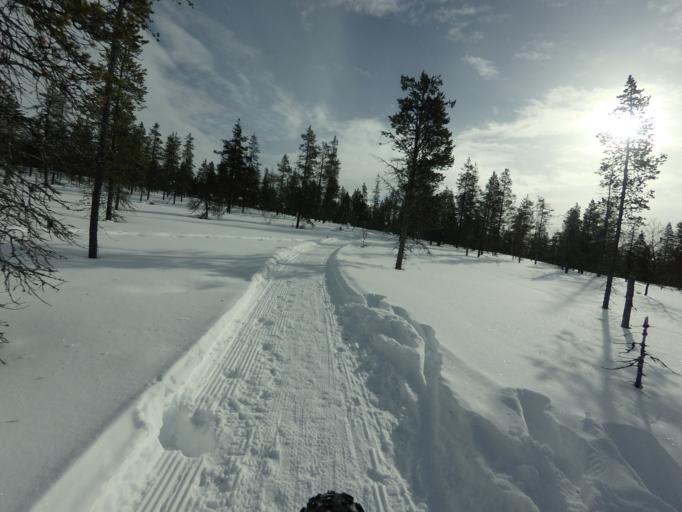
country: FI
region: Lapland
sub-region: Pohjois-Lappi
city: Ivalo
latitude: 68.3451
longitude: 27.4306
